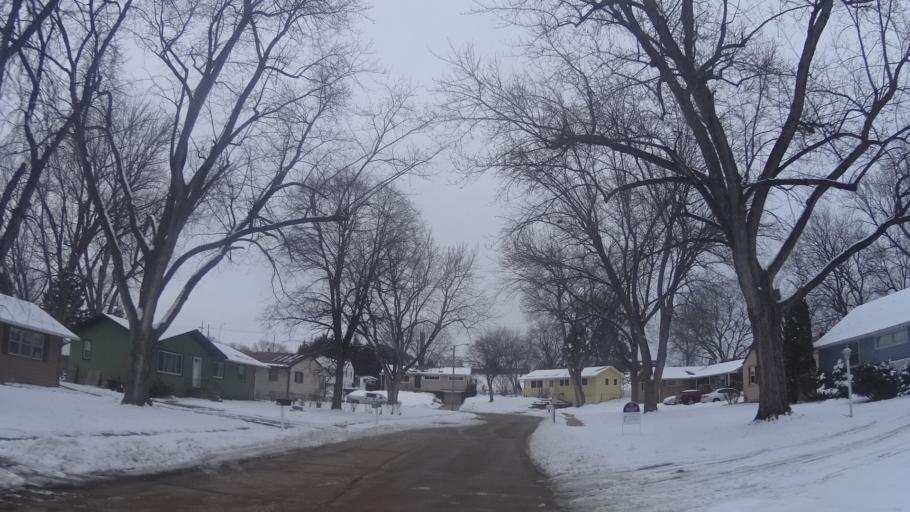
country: US
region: Nebraska
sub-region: Sarpy County
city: Offutt Air Force Base
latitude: 41.1390
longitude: -95.9177
